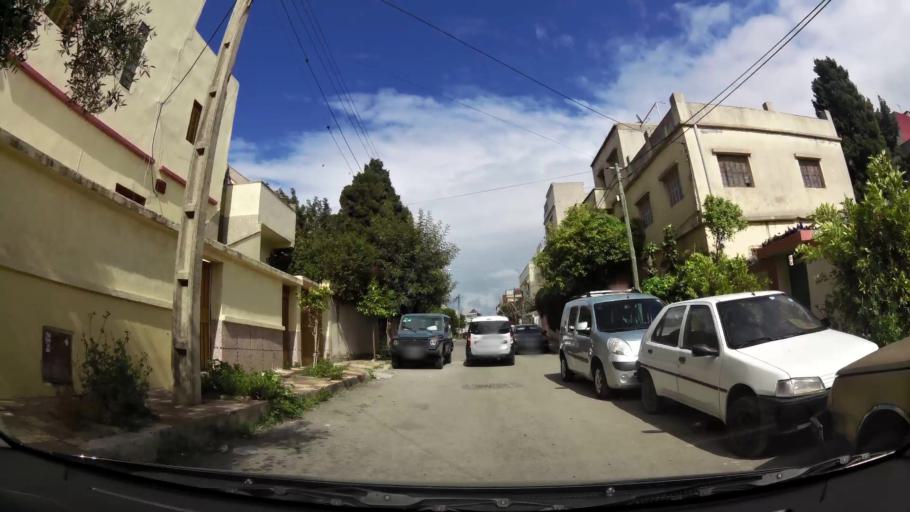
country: MA
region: Tanger-Tetouan
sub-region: Tanger-Assilah
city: Tangier
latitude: 35.7633
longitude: -5.8093
